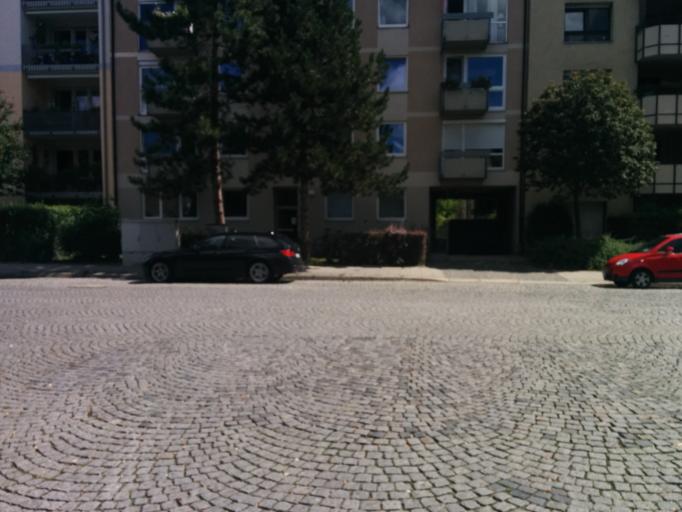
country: DE
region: Bavaria
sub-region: Upper Bavaria
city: Munich
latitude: 48.1690
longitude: 11.5757
